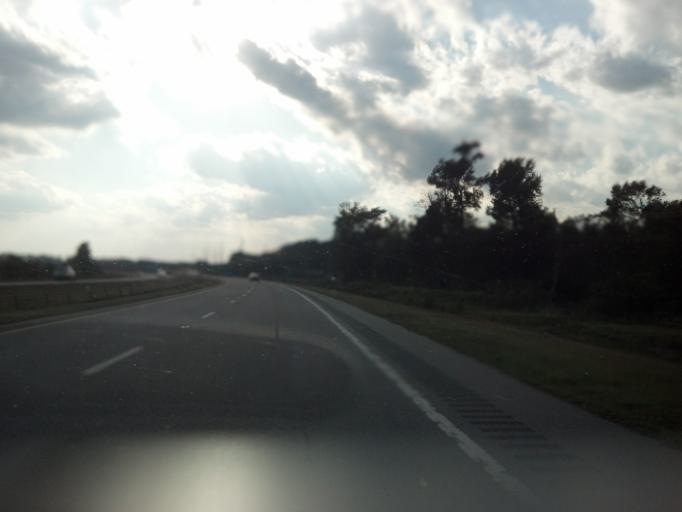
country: US
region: North Carolina
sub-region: Pitt County
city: Greenville
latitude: 35.6651
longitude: -77.4026
